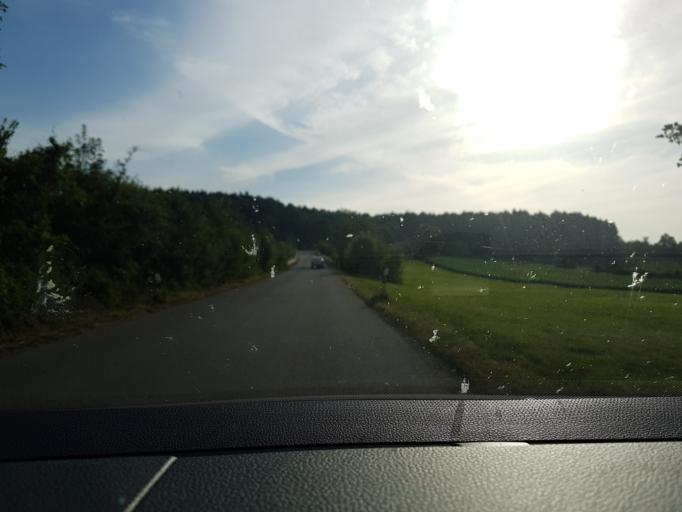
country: DE
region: Bavaria
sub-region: Upper Bavaria
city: Ainring
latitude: 47.8610
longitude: 12.9063
